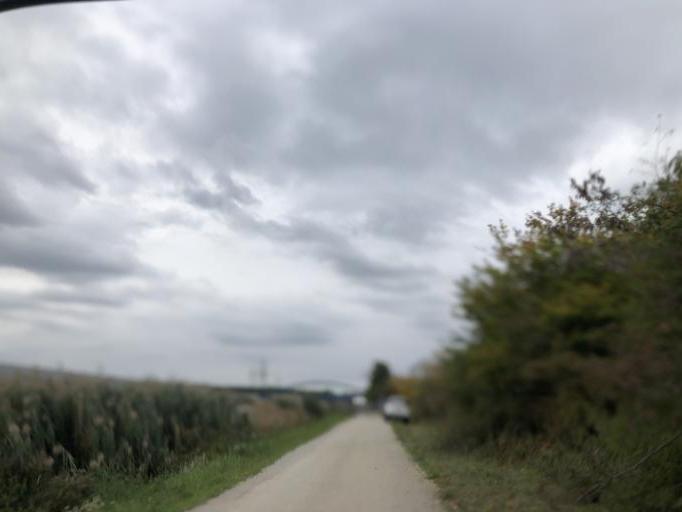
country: DE
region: Bavaria
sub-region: Regierungsbezirk Mittelfranken
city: Erlangen
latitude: 49.5648
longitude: 10.9700
